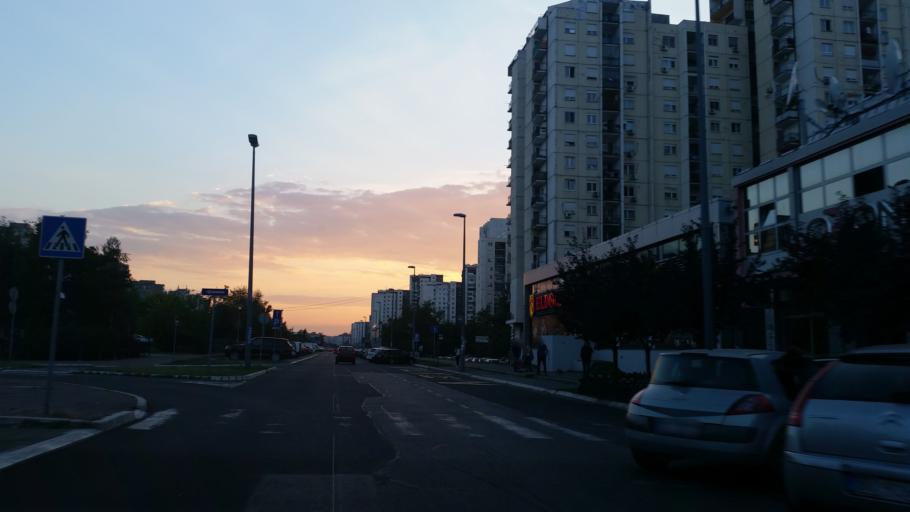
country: RS
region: Central Serbia
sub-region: Belgrade
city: Zemun
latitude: 44.8068
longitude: 20.3822
